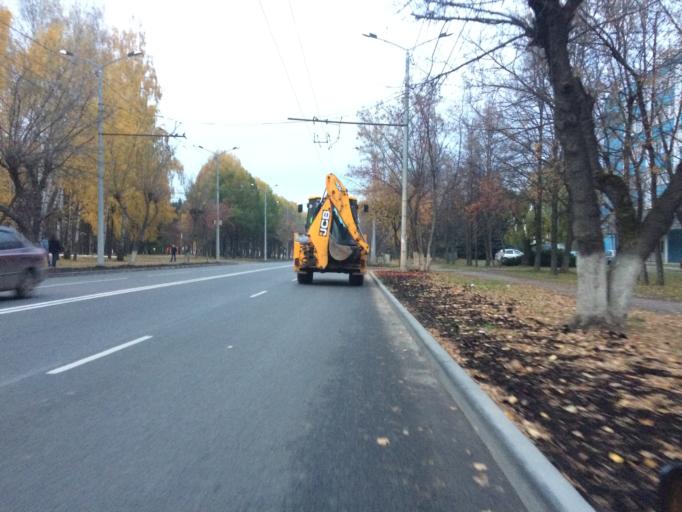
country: RU
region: Mariy-El
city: Yoshkar-Ola
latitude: 56.6111
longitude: 47.8801
